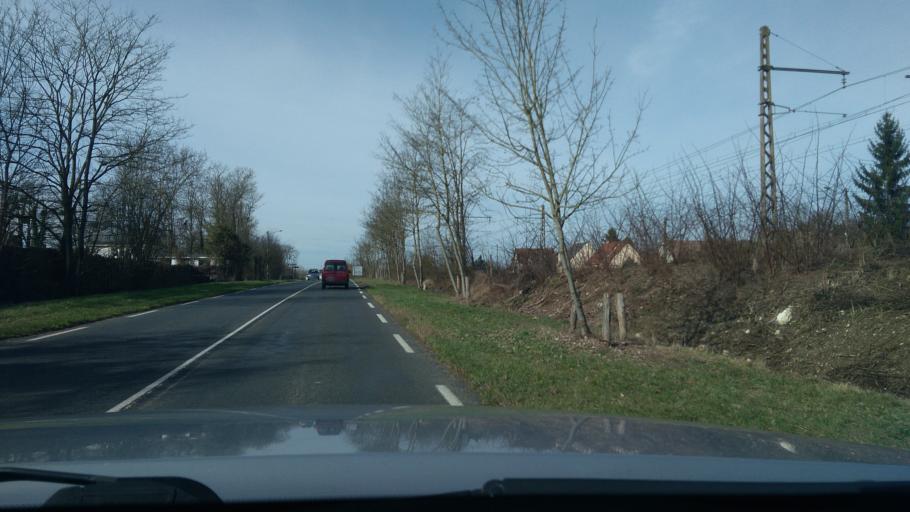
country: FR
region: Ile-de-France
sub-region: Departement de Seine-et-Marne
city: Livry-sur-Seine
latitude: 48.5061
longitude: 2.6818
